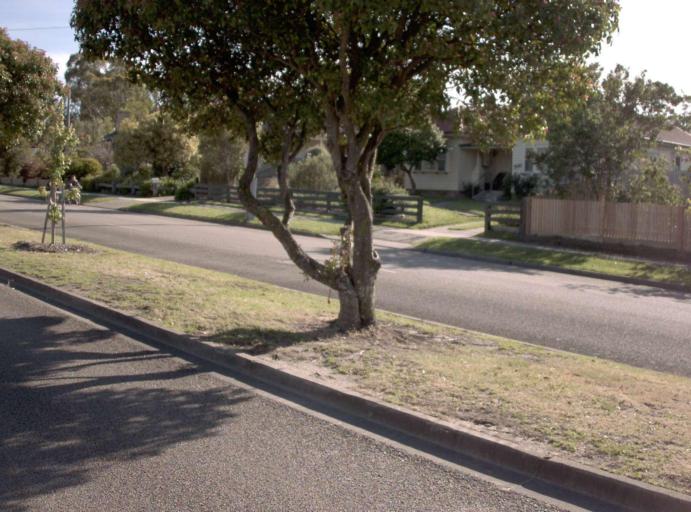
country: AU
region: Victoria
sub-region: East Gippsland
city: Lakes Entrance
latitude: -37.7010
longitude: 148.4563
